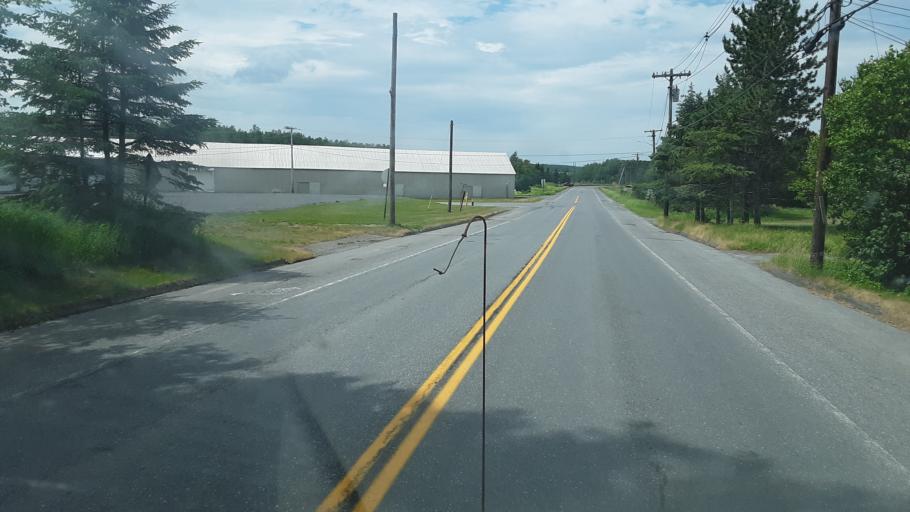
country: US
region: Maine
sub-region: Aroostook County
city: Fort Fairfield
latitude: 46.7750
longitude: -67.8398
